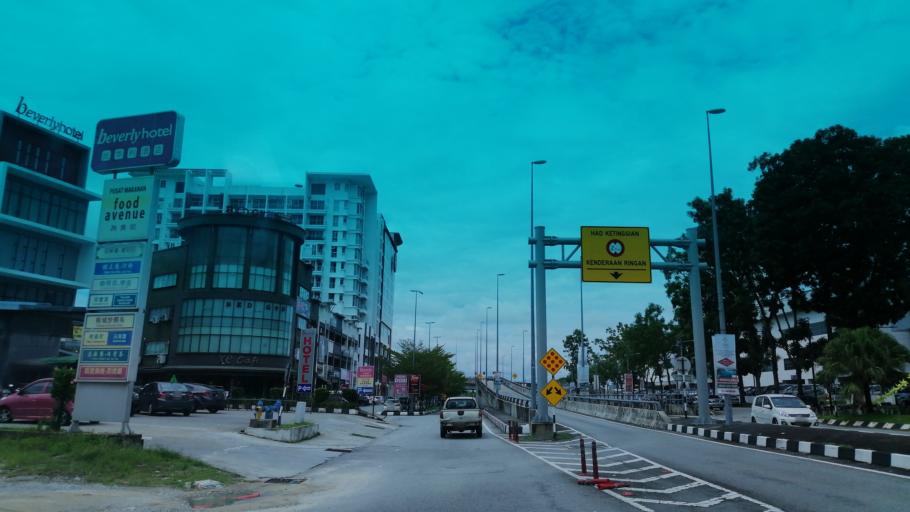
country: MY
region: Perak
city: Taiping
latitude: 4.8651
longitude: 100.7310
